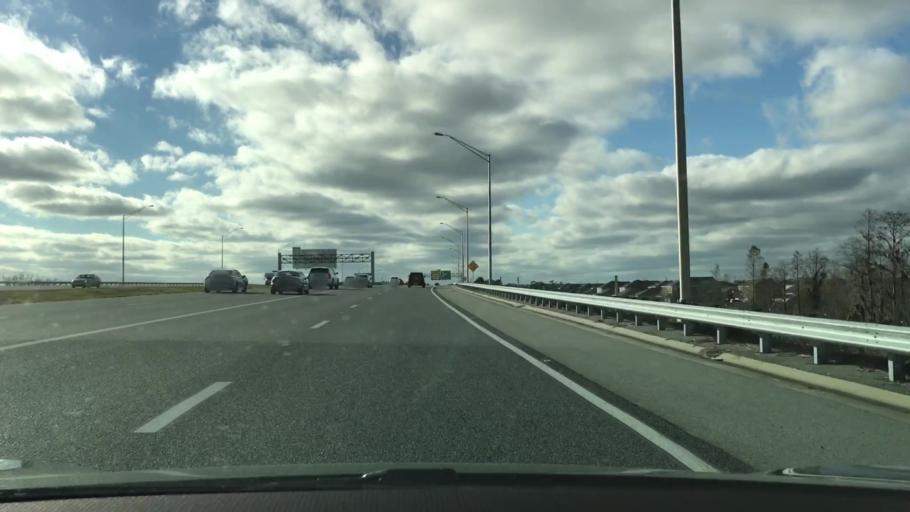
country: US
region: Florida
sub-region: Osceola County
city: Buenaventura Lakes
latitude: 28.3674
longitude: -81.3232
